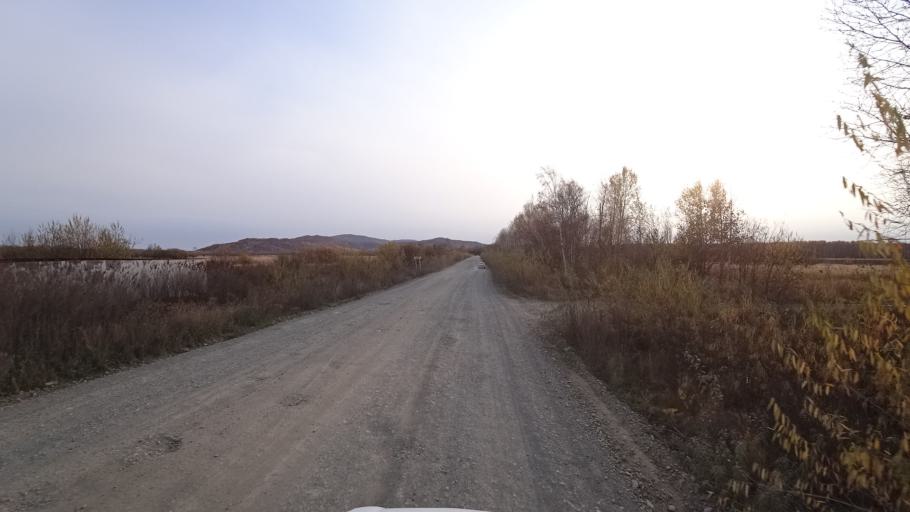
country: RU
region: Khabarovsk Krai
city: Amursk
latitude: 50.0719
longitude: 136.4883
